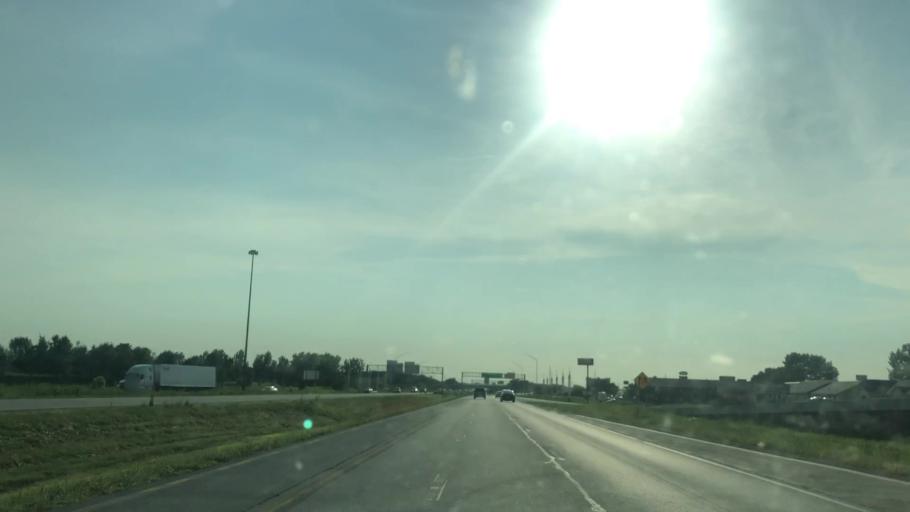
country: US
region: Iowa
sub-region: Story County
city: Ames
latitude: 42.0076
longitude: -93.5746
